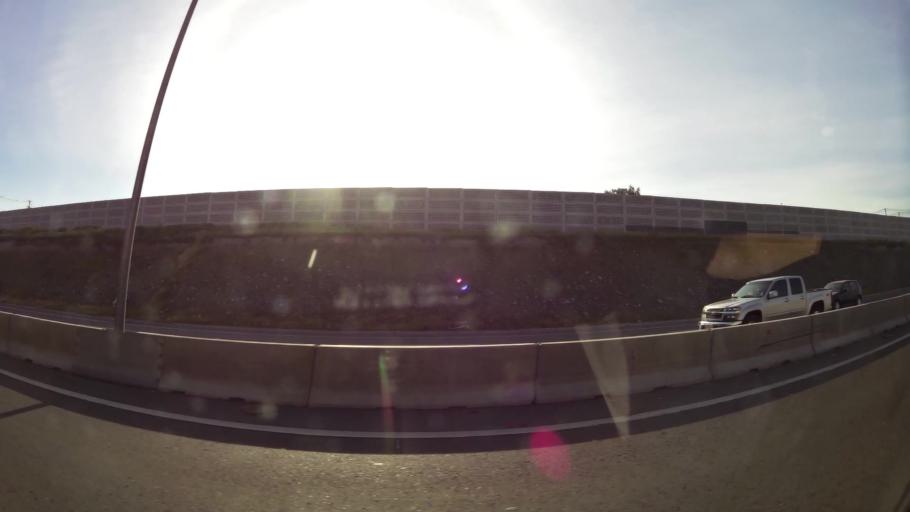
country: CL
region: Santiago Metropolitan
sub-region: Provincia de Santiago
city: La Pintana
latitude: -33.5846
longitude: -70.6105
